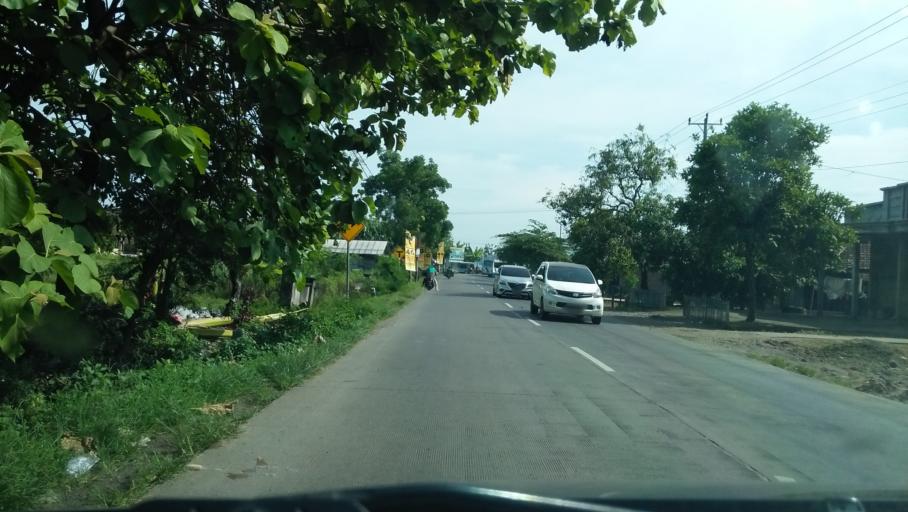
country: ID
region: Central Java
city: Welahan
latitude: -6.8550
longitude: 110.7061
